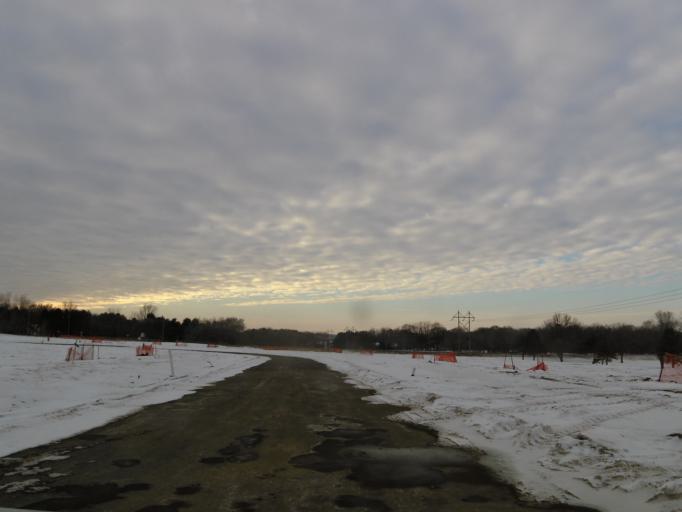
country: US
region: Minnesota
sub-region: Washington County
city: Lake Elmo
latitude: 44.9559
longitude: -92.8805
